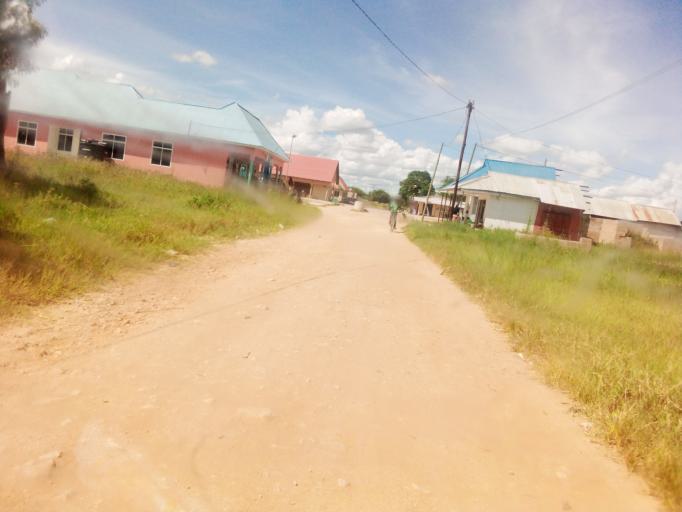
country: TZ
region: Dodoma
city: Kisasa
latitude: -6.1622
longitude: 35.7680
